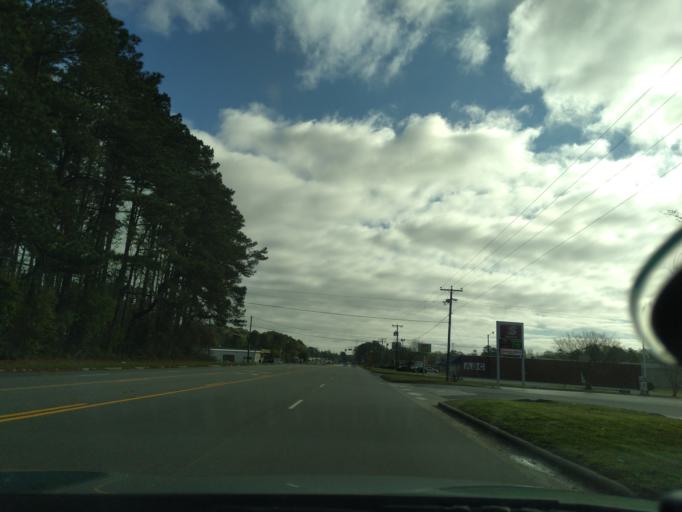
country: US
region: North Carolina
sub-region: Washington County
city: Plymouth
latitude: 35.8616
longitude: -76.7351
